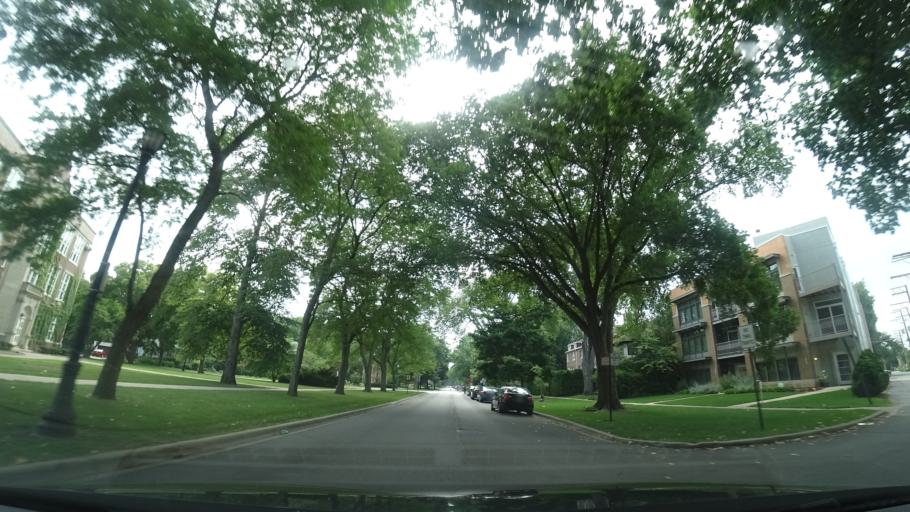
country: US
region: Illinois
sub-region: Cook County
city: Evanston
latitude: 42.0622
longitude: -87.6979
